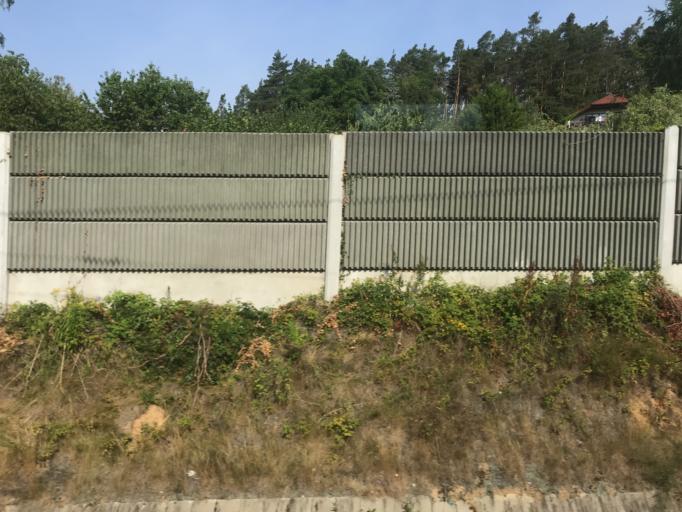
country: CZ
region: Central Bohemia
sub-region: Okres Benesov
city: Cercany
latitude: 49.8695
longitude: 14.7156
